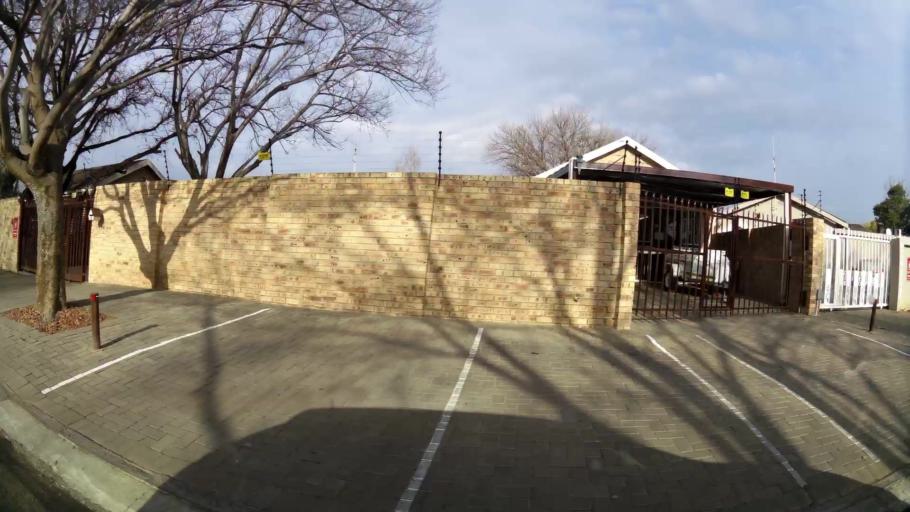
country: ZA
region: Orange Free State
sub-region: Mangaung Metropolitan Municipality
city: Bloemfontein
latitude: -29.1212
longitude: 26.1766
